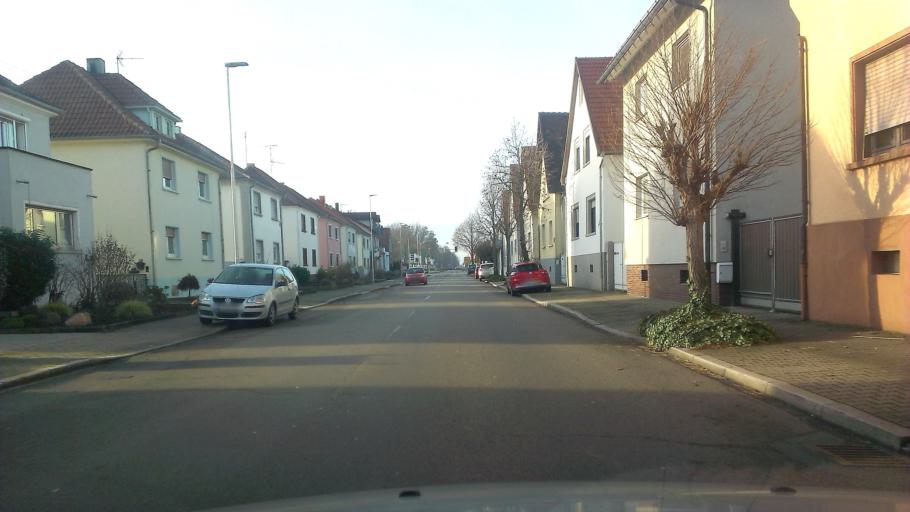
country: DE
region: Baden-Wuerttemberg
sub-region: Karlsruhe Region
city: Waghausel
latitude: 49.2448
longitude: 8.5388
